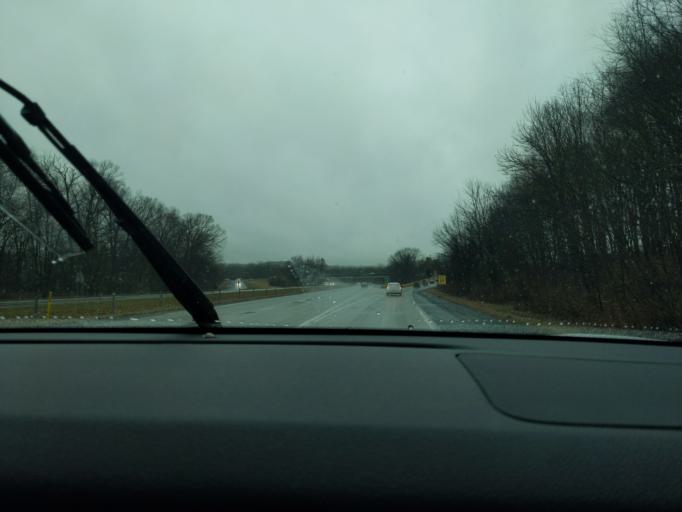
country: US
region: Pennsylvania
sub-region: Bucks County
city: Doylestown
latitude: 40.3287
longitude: -75.1372
